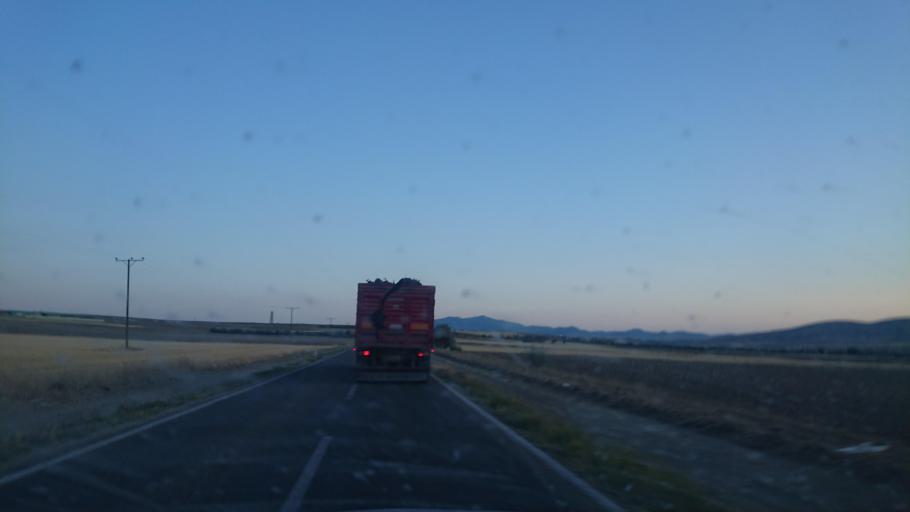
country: TR
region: Aksaray
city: Balci
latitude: 38.8104
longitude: 34.1323
